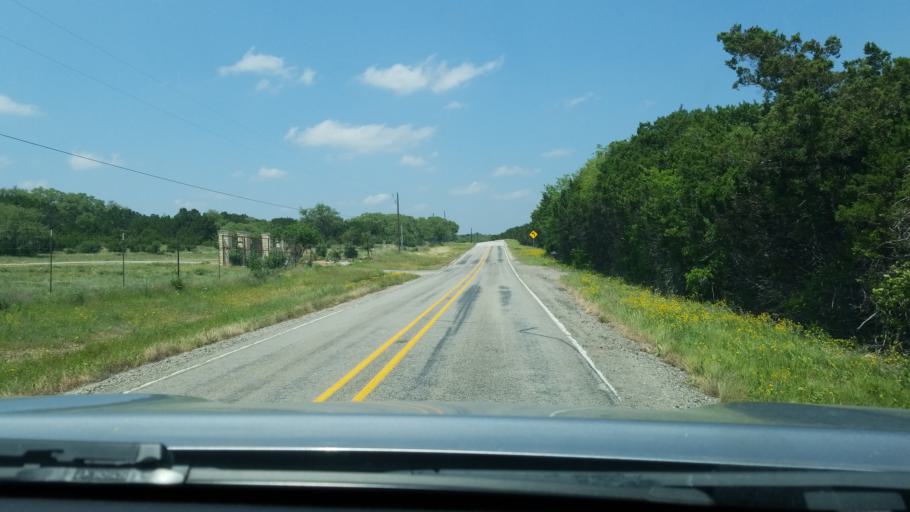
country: US
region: Texas
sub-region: Hays County
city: Woodcreek
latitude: 30.0880
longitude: -98.2285
